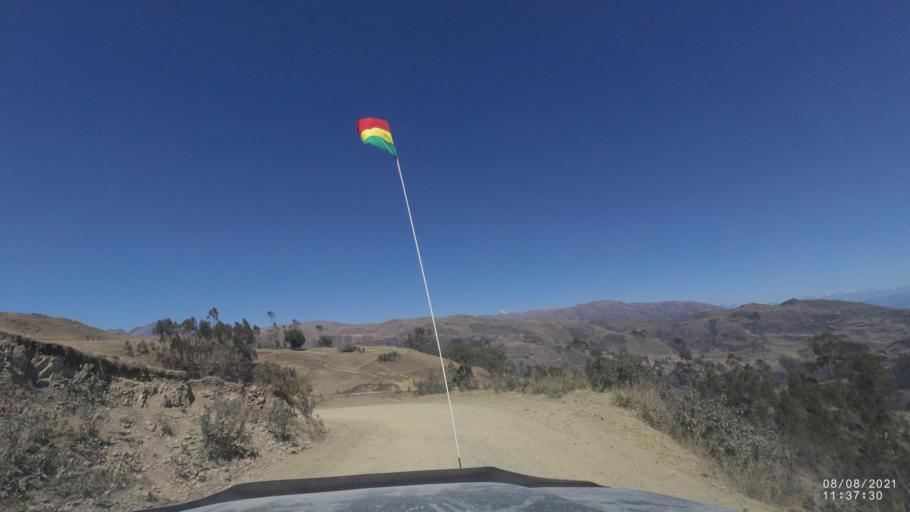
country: BO
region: Cochabamba
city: Colchani
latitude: -16.7859
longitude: -66.6480
